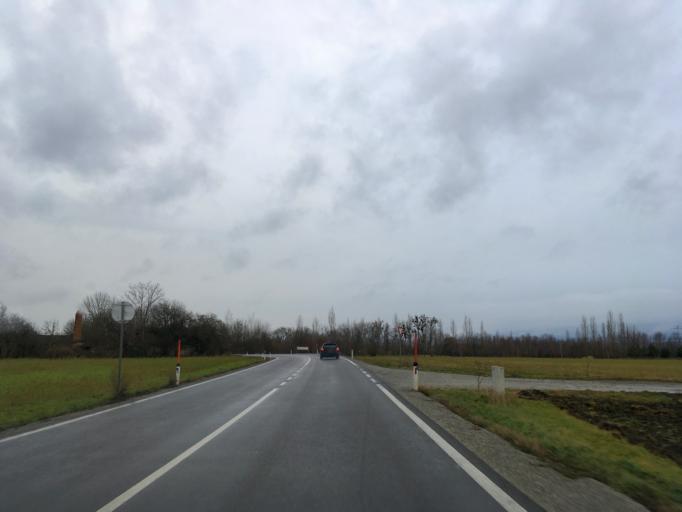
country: AT
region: Lower Austria
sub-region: Politischer Bezirk Wien-Umgebung
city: Ebergassing
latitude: 48.0399
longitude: 16.5366
